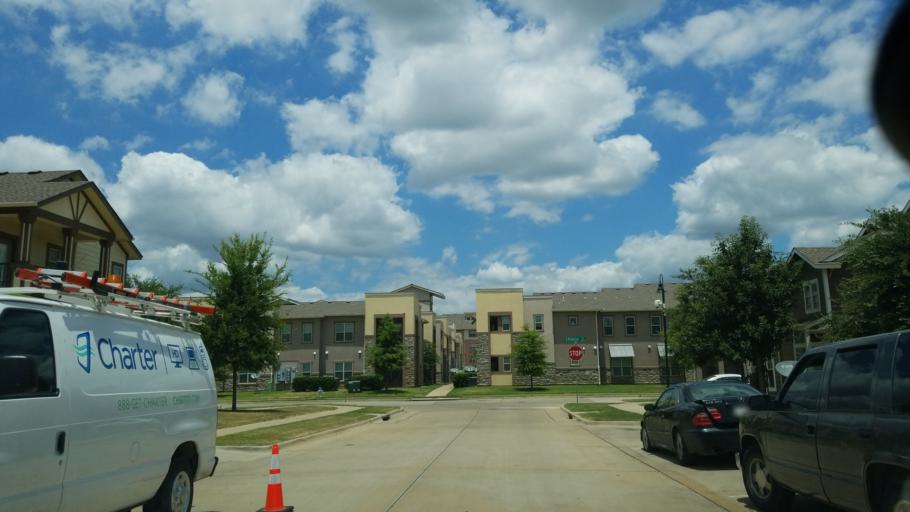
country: US
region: Texas
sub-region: Dallas County
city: Dallas
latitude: 32.7355
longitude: -96.7553
